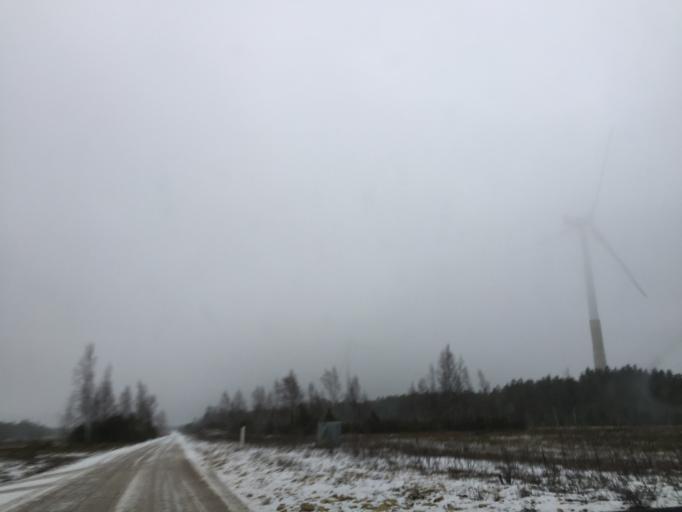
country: EE
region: Laeaene
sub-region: Haapsalu linn
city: Haapsalu
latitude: 58.6288
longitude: 23.5318
